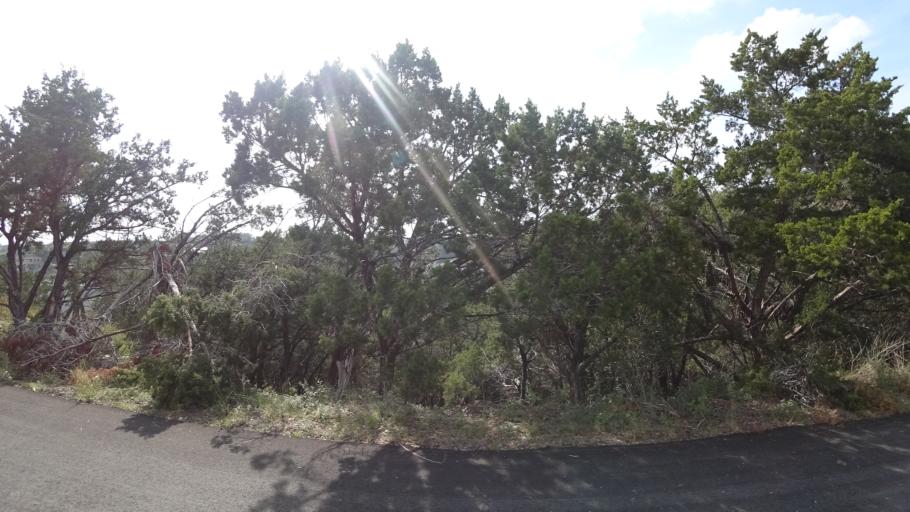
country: US
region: Texas
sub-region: Travis County
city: Hudson Bend
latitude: 30.3838
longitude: -97.9258
